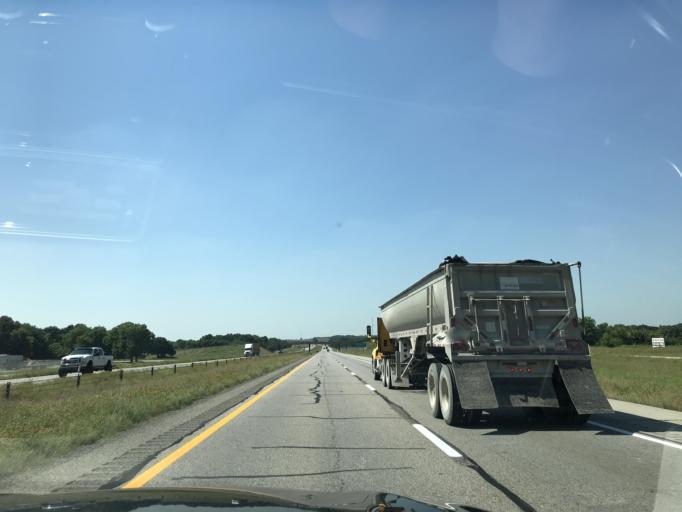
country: US
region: Texas
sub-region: Johnson County
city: Grandview
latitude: 32.3017
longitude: -97.1814
